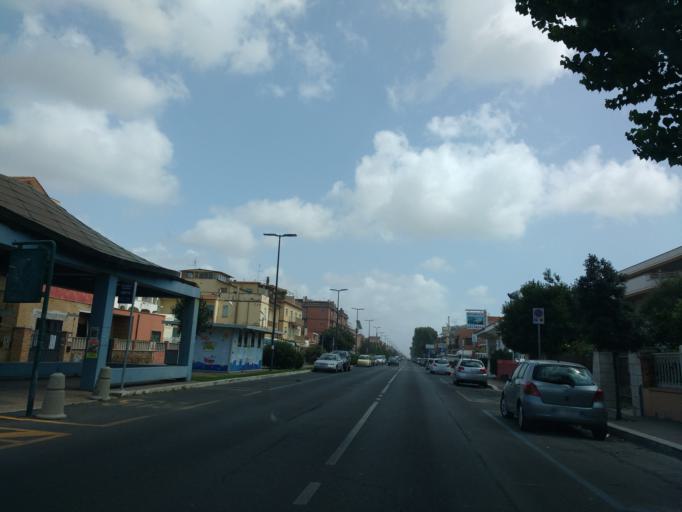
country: IT
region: Latium
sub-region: Citta metropolitana di Roma Capitale
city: Torvaianica
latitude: 41.6238
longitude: 12.4594
